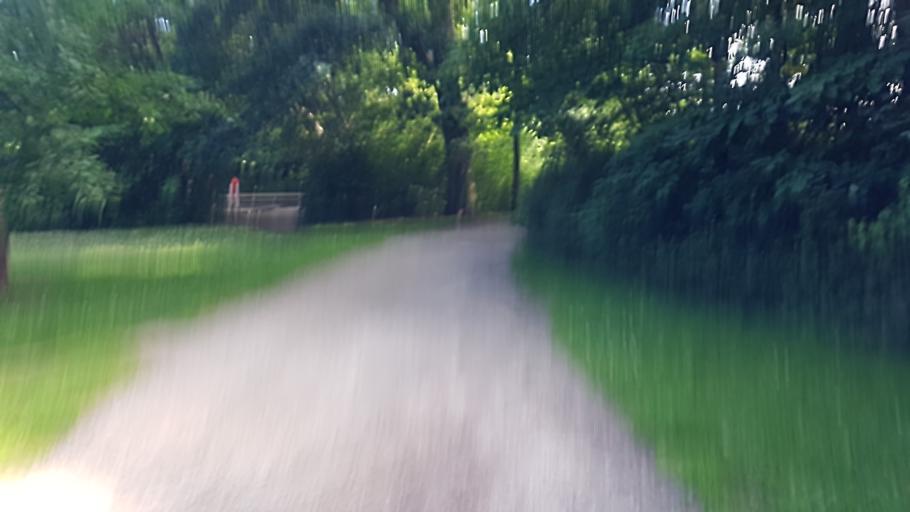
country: SE
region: Skane
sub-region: Lunds Kommun
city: Lund
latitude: 55.7070
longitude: 13.2116
